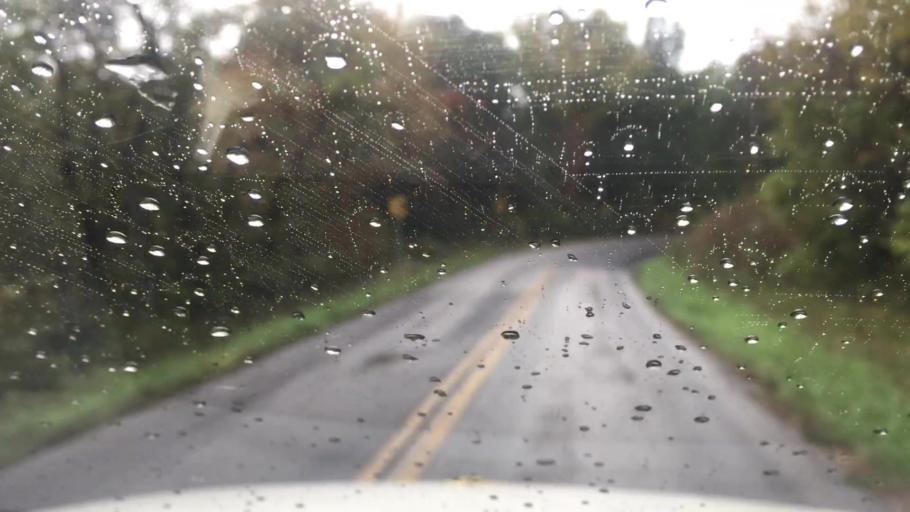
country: US
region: Missouri
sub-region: Boone County
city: Columbia
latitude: 38.9336
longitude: -92.4890
